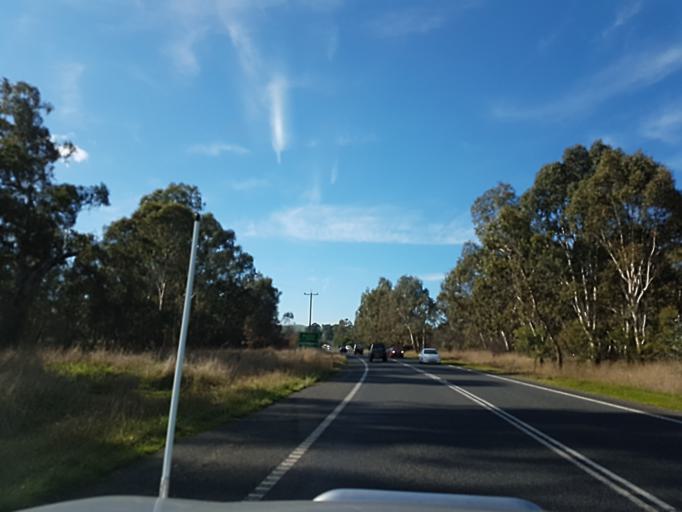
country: AU
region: Victoria
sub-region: Murrindindi
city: Alexandra
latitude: -37.1514
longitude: 145.5803
